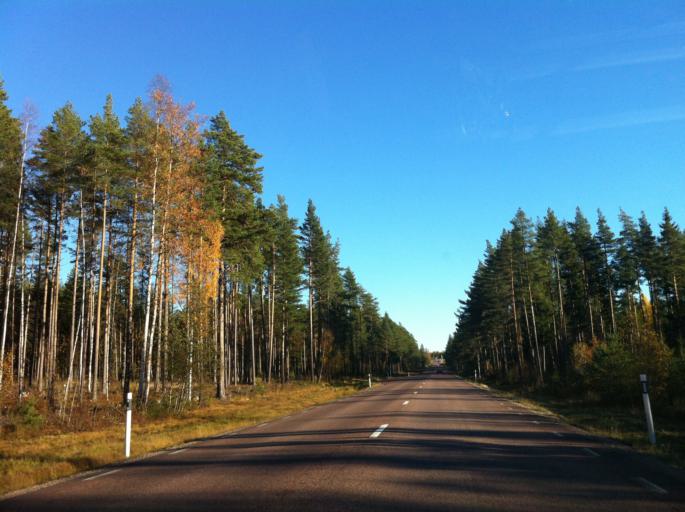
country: SE
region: Dalarna
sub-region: Leksand Municipality
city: Siljansnas
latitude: 60.9285
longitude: 14.7990
